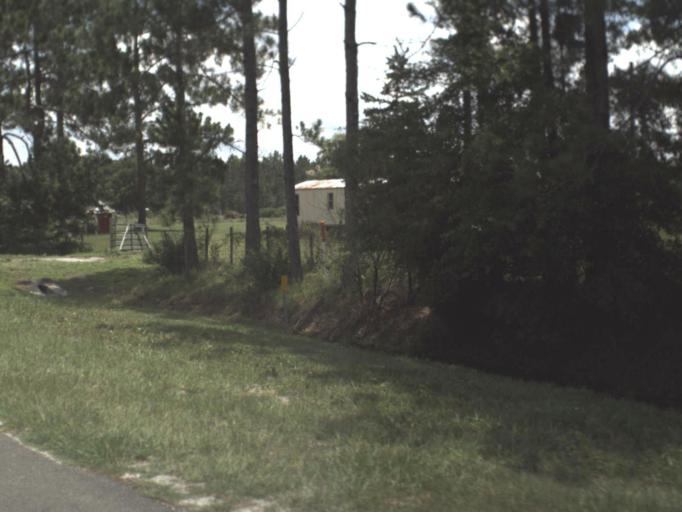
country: US
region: Florida
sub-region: Union County
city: Lake Butler
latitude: 29.9887
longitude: -82.3552
